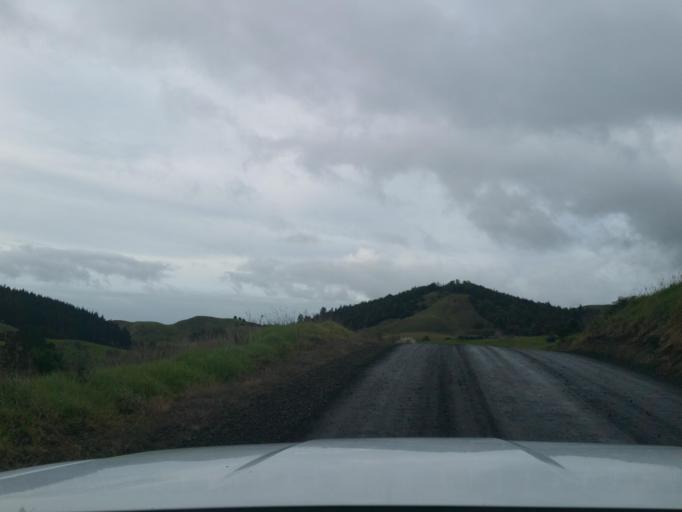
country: NZ
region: Northland
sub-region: Kaipara District
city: Dargaville
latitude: -35.8201
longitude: 173.8154
